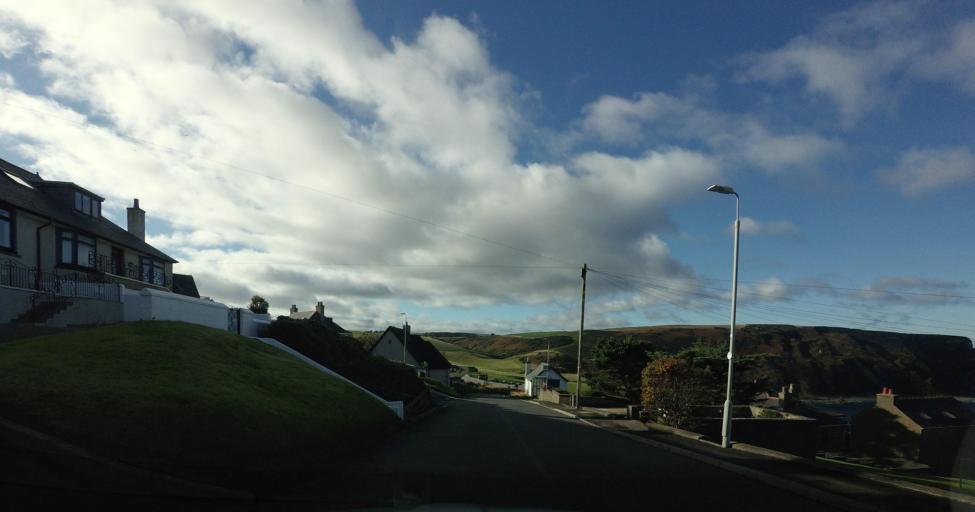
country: GB
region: Scotland
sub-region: Aberdeenshire
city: Macduff
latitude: 57.6701
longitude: -2.3360
